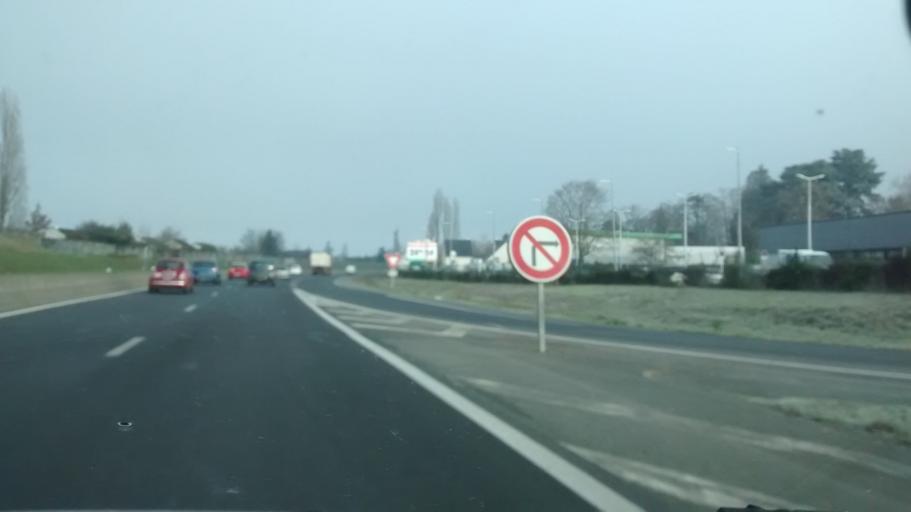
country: FR
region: Centre
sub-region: Departement d'Indre-et-Loire
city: Joue-les-Tours
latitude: 47.3581
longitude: 0.6458
